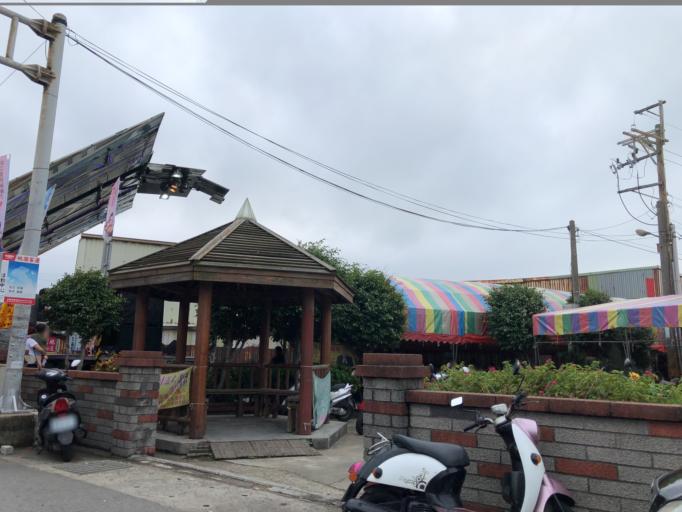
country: TW
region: Taiwan
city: Taoyuan City
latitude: 25.1086
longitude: 121.2418
